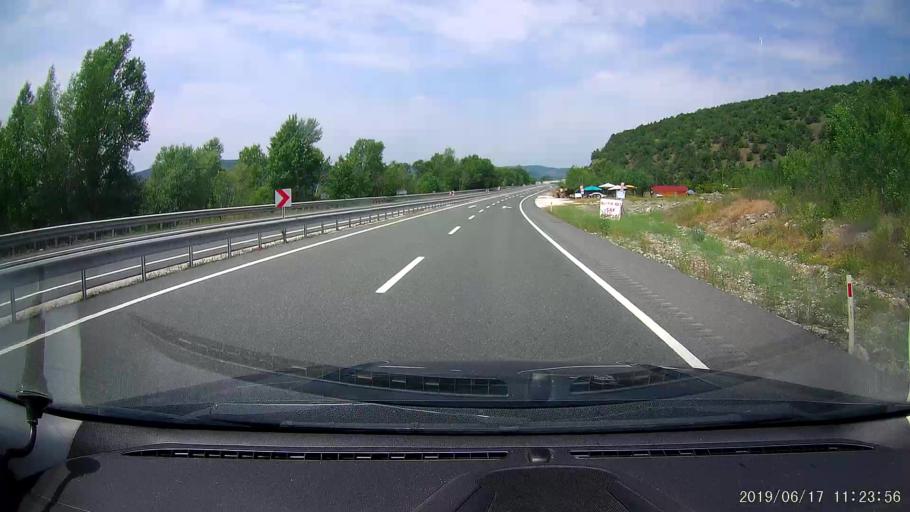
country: TR
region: Cankiri
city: Ilgaz
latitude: 40.8839
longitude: 33.7183
